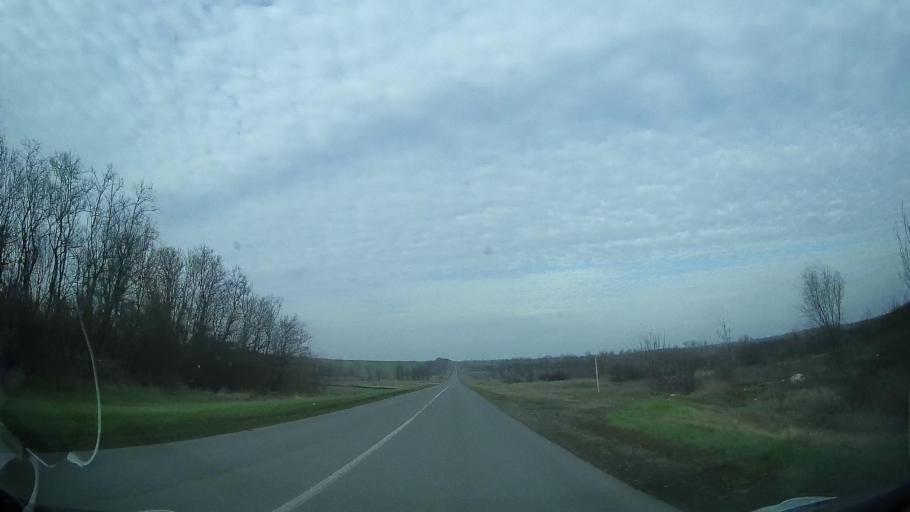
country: RU
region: Rostov
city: Zernograd
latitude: 46.8944
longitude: 40.3389
